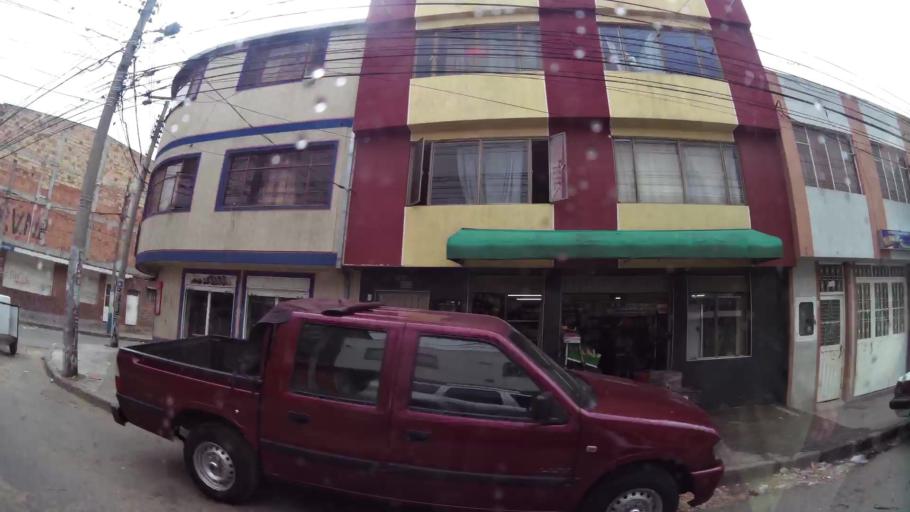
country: CO
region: Bogota D.C.
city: Bogota
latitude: 4.6030
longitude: -74.1416
